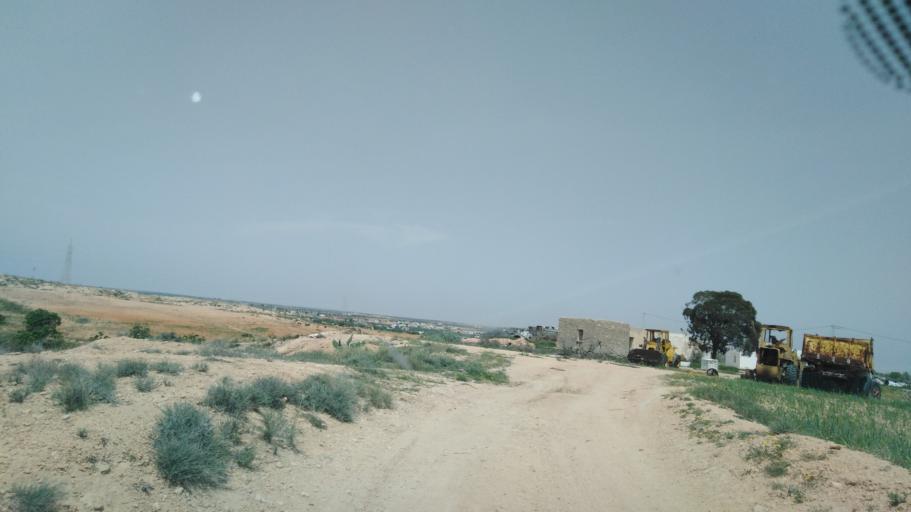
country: TN
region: Safaqis
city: Sfax
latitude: 34.7206
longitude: 10.5663
